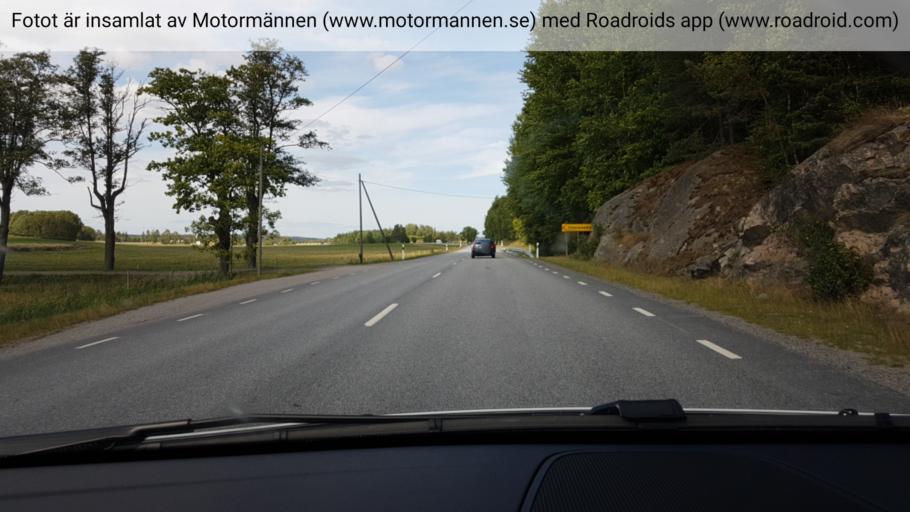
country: SE
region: Stockholm
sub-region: Sodertalje Kommun
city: Pershagen
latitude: 59.0546
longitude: 17.6110
